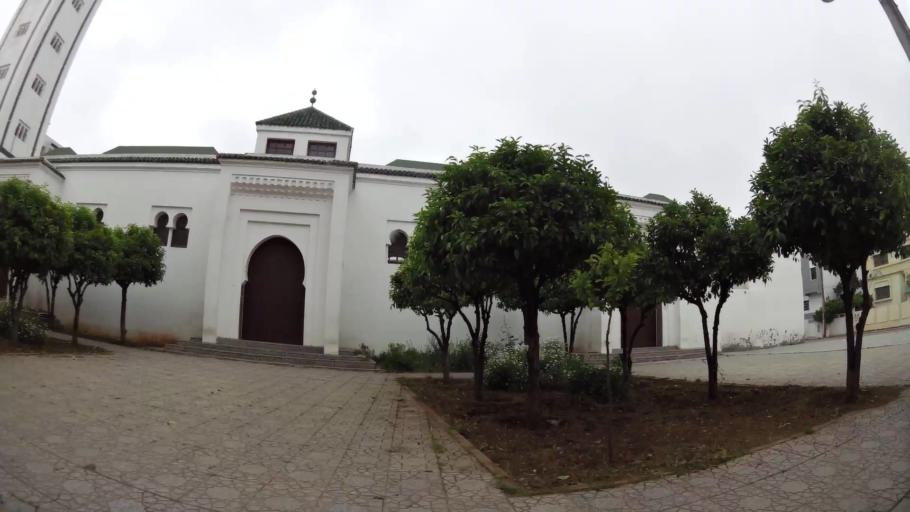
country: MA
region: Fes-Boulemane
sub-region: Fes
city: Fes
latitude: 34.0301
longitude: -5.0082
